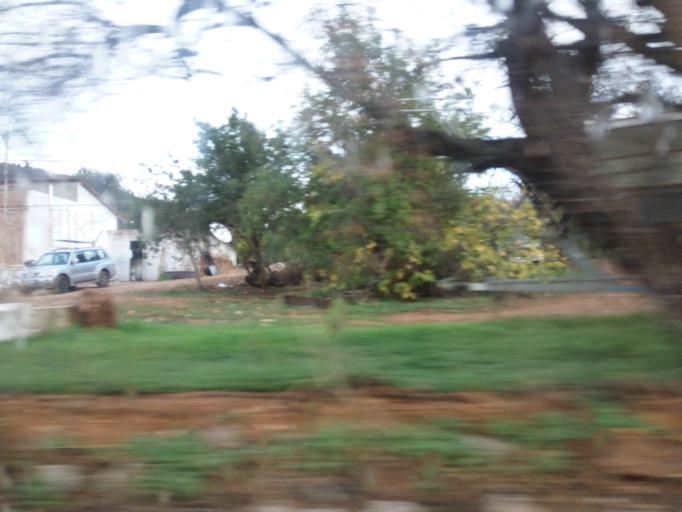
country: PT
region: Faro
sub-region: Faro
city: Santa Barbara de Nexe
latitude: 37.1056
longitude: -7.9747
